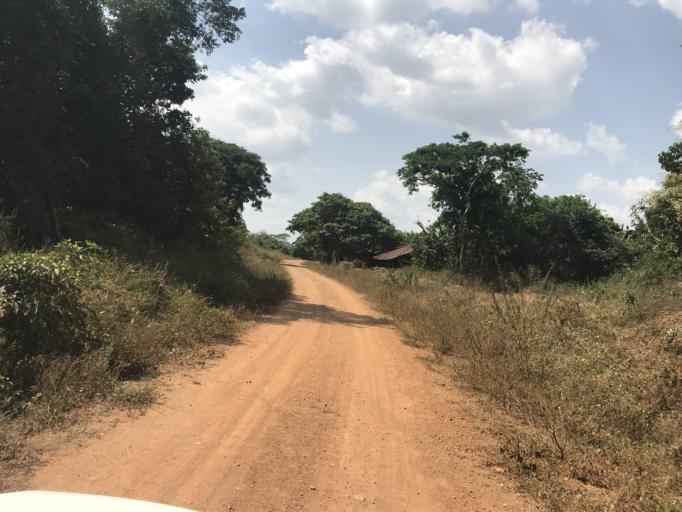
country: NG
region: Osun
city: Ifon
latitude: 7.9779
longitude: 4.5244
